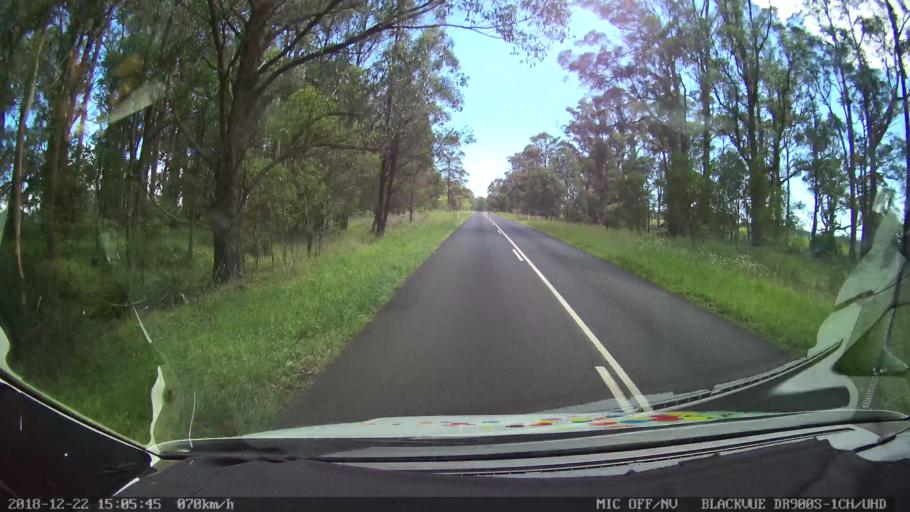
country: AU
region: New South Wales
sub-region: Bellingen
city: Dorrigo
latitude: -30.2871
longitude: 152.4332
